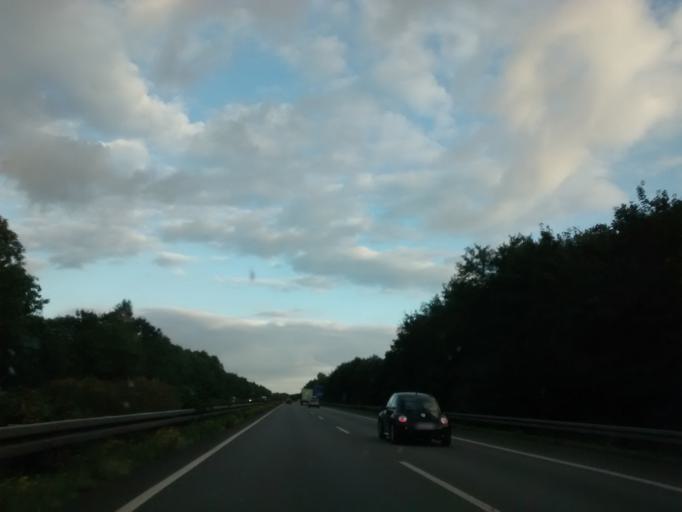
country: DE
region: North Rhine-Westphalia
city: Ibbenburen
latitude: 52.2613
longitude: 7.6927
